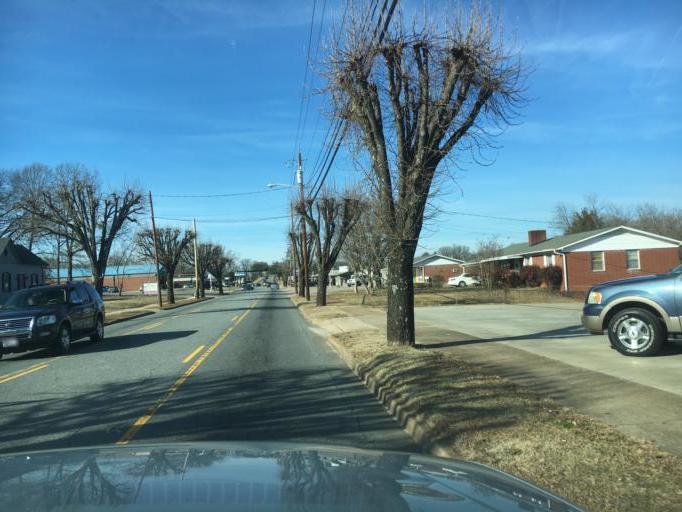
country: US
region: North Carolina
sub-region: Rutherford County
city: Forest City
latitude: 35.3250
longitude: -81.8609
